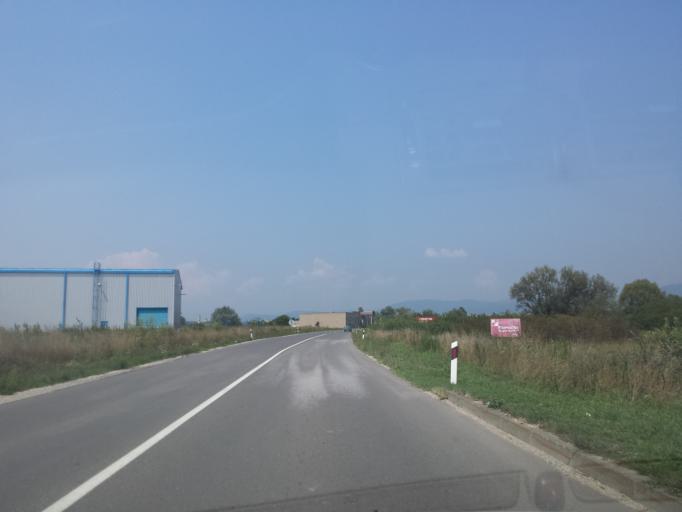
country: HR
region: Zagrebacka
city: Jastrebarsko
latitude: 45.6522
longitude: 15.6595
